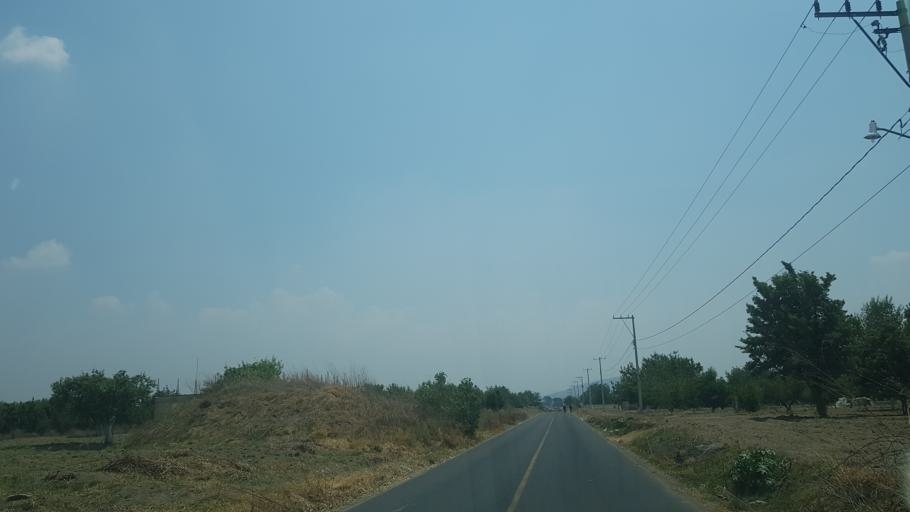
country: MX
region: Puebla
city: San Andres Calpan
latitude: 19.0979
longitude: -98.4196
